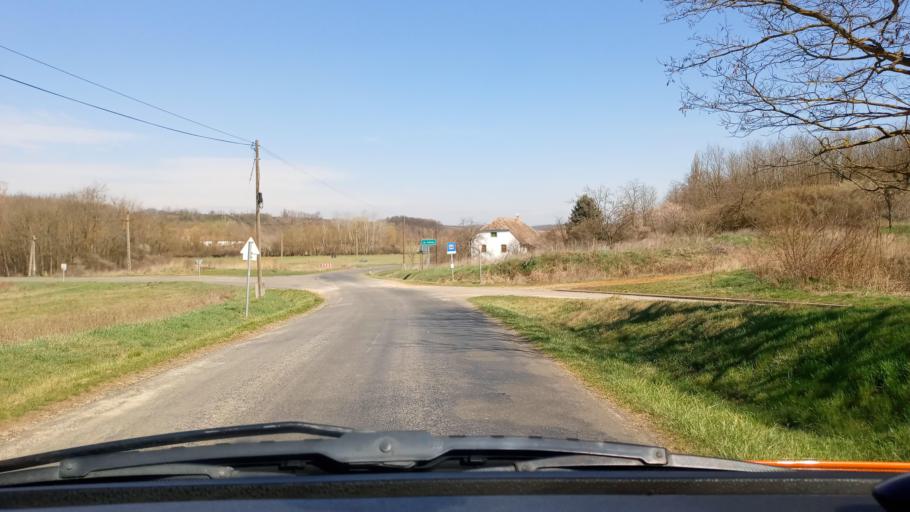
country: HU
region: Baranya
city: Boly
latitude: 46.0563
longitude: 18.4568
